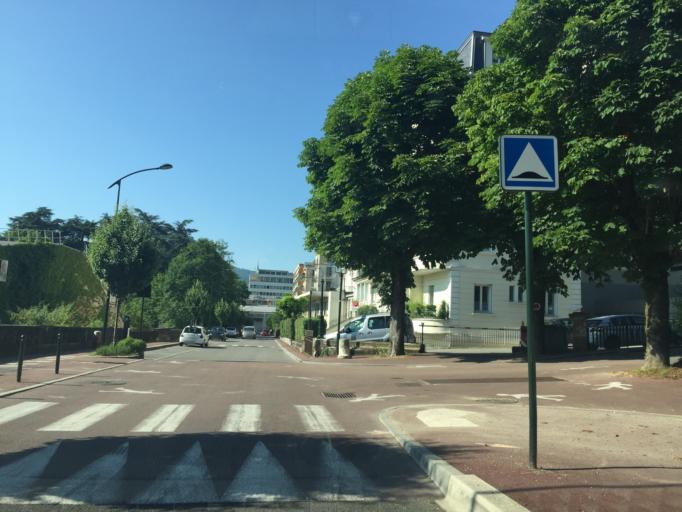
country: FR
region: Rhone-Alpes
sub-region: Departement de la Savoie
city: Aix-les-Bains
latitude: 45.6852
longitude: 5.9168
